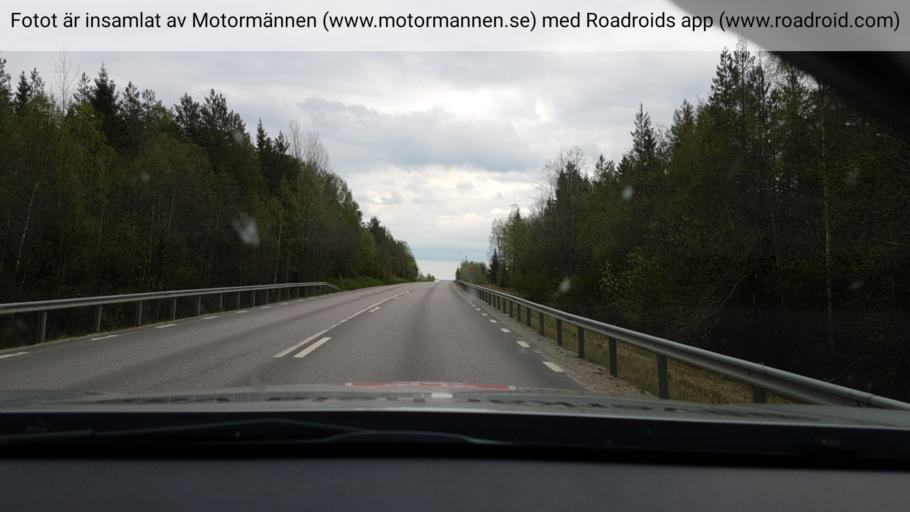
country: SE
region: Vaesterbotten
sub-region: Vannas Kommun
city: Vaennaes
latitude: 63.9178
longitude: 19.6449
